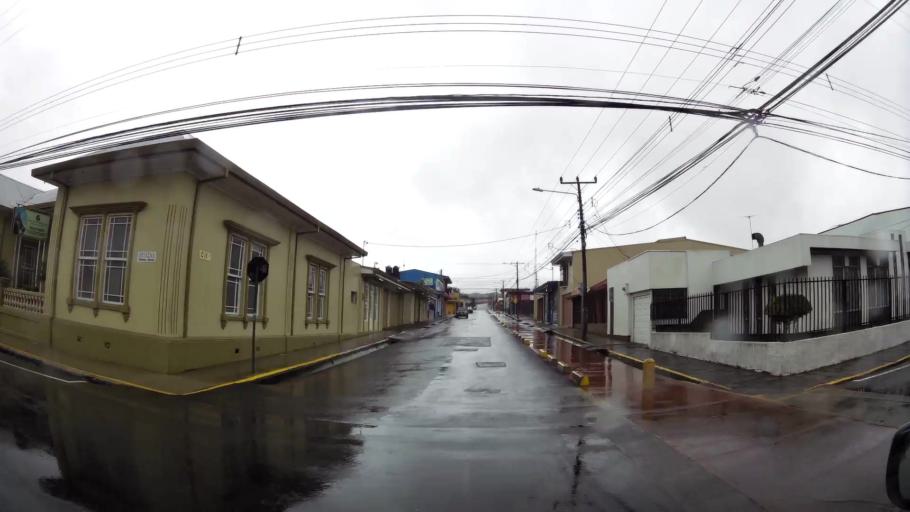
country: CR
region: Cartago
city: Cartago
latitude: 9.8654
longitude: -83.9256
